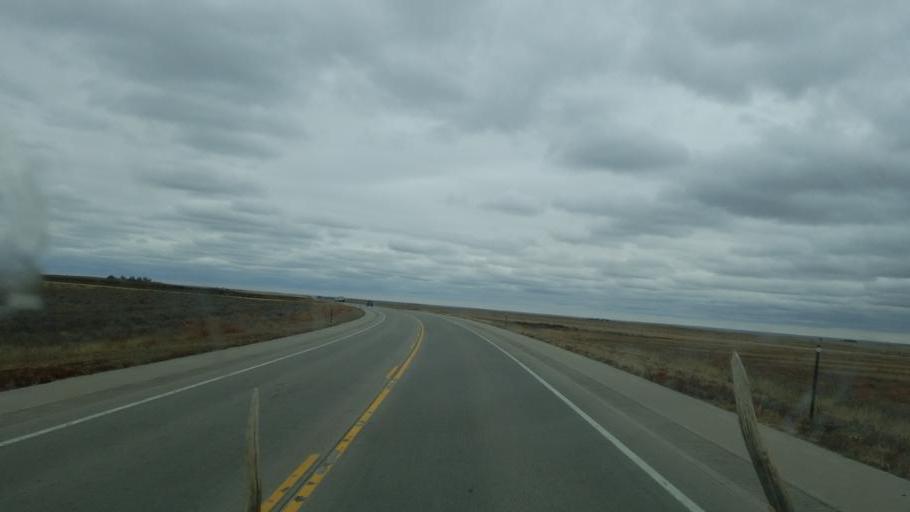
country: US
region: Colorado
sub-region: Kiowa County
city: Eads
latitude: 38.6896
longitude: -102.7759
